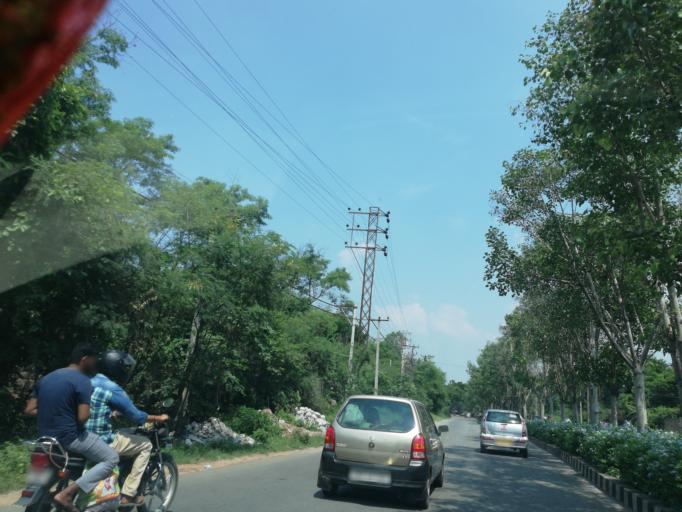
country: IN
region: Telangana
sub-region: Medak
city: Serilingampalle
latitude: 17.4635
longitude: 78.3348
